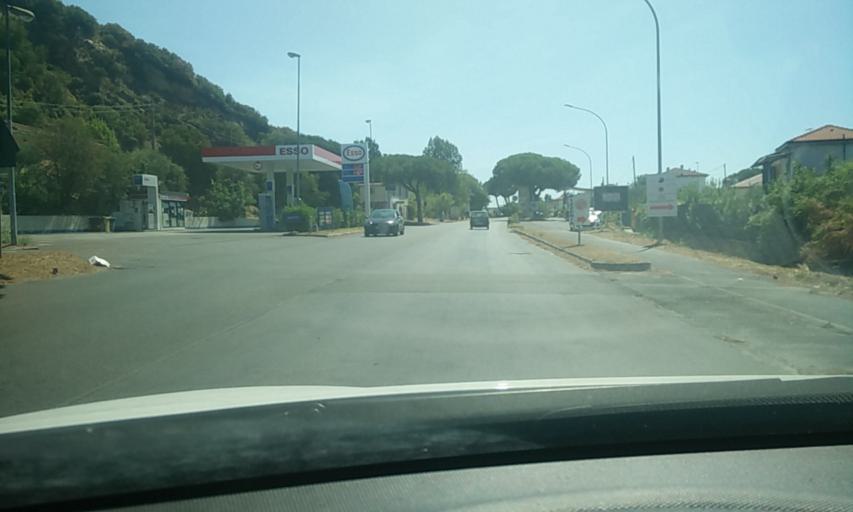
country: IT
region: Tuscany
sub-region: Provincia di Massa-Carrara
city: Massa
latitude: 44.0391
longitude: 10.0951
